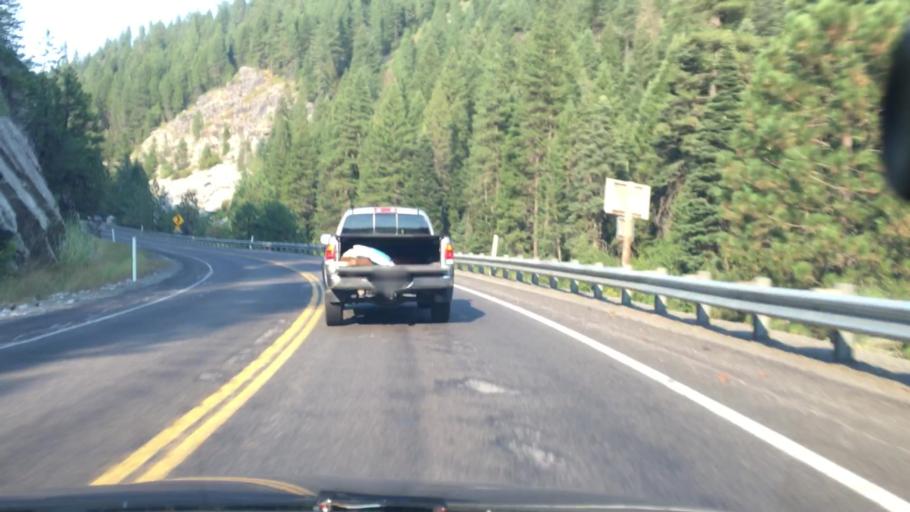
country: US
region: Idaho
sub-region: Valley County
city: Cascade
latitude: 44.2444
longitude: -116.0987
